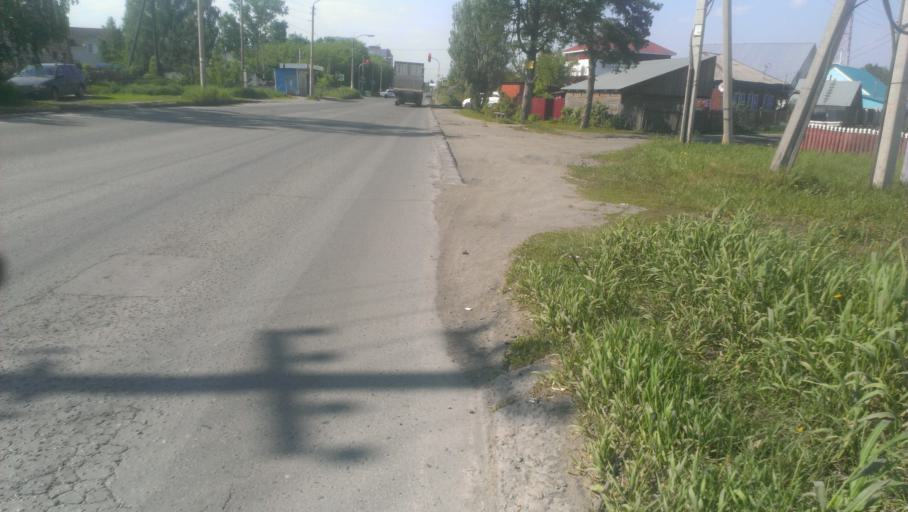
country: RU
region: Altai Krai
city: Novoaltaysk
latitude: 53.4063
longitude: 83.9445
